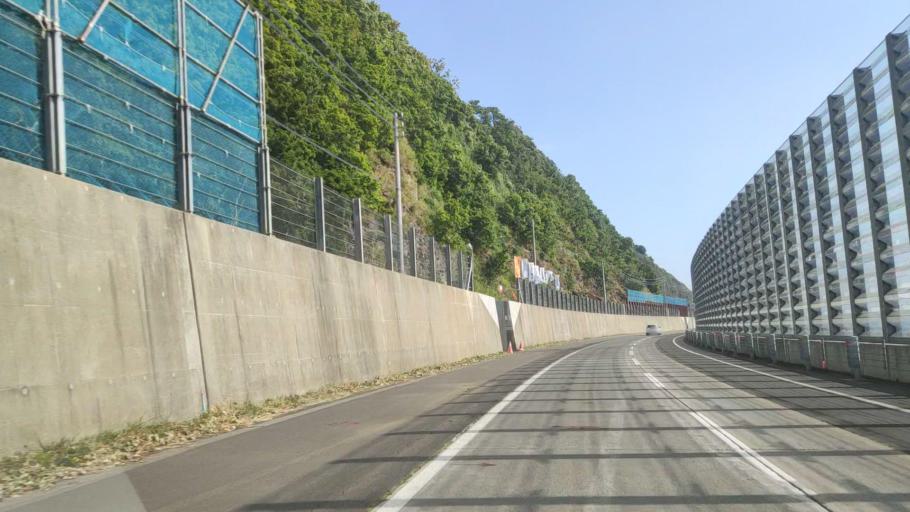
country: JP
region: Hokkaido
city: Rumoi
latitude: 43.6618
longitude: 141.3504
